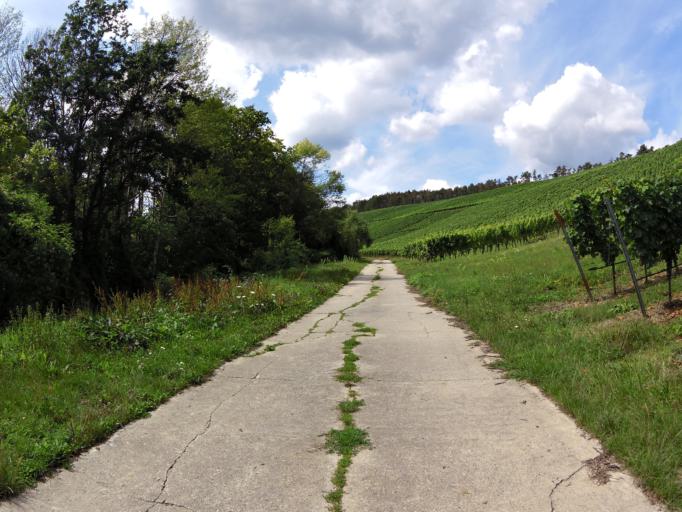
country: DE
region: Bavaria
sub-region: Regierungsbezirk Unterfranken
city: Erlabrunn
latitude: 49.8459
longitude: 9.8402
